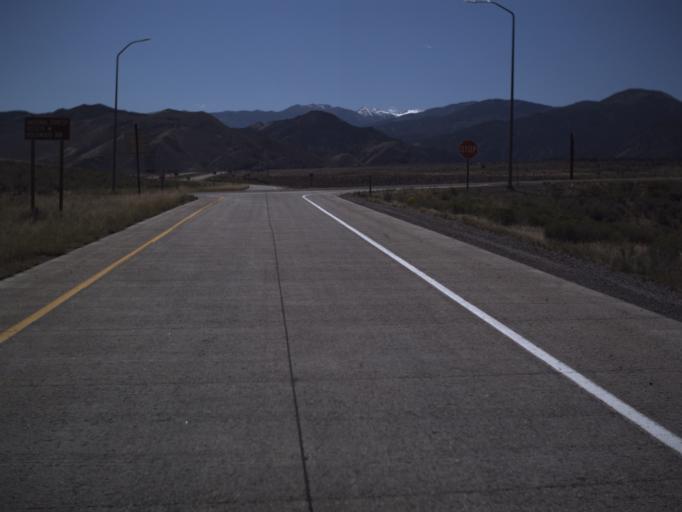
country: US
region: Utah
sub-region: Sevier County
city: Monroe
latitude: 38.6260
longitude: -112.2269
